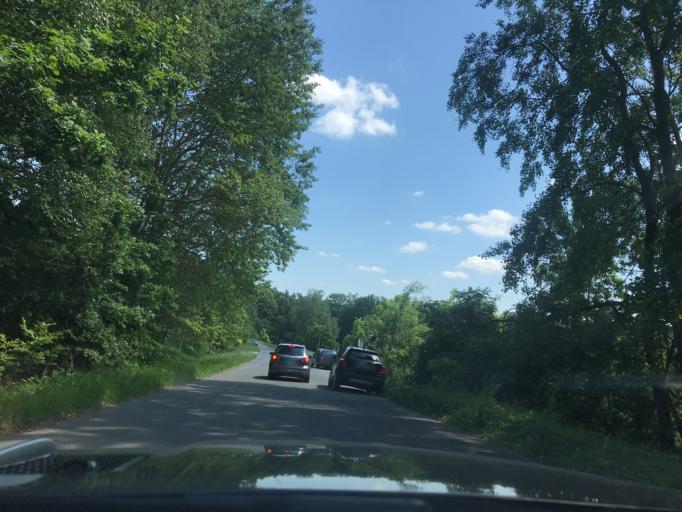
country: DE
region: Thuringia
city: Neuhaus
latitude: 50.7407
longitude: 10.9468
